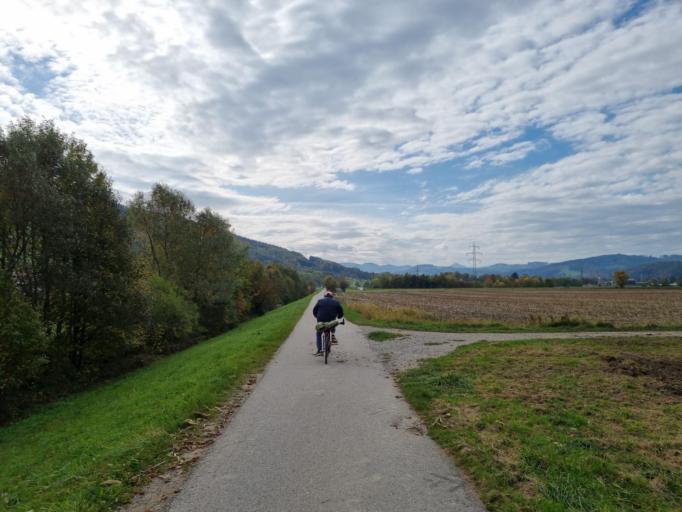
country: AT
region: Lower Austria
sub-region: Politischer Bezirk Sankt Polten
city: Wilhelmsburg
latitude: 48.1159
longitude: 15.6215
